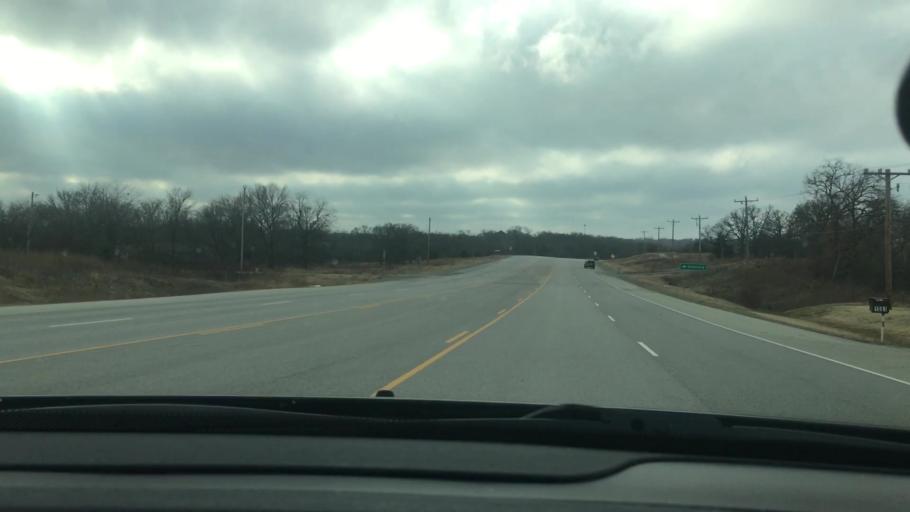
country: US
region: Oklahoma
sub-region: Bryan County
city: Durant
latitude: 34.0535
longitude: -96.3729
